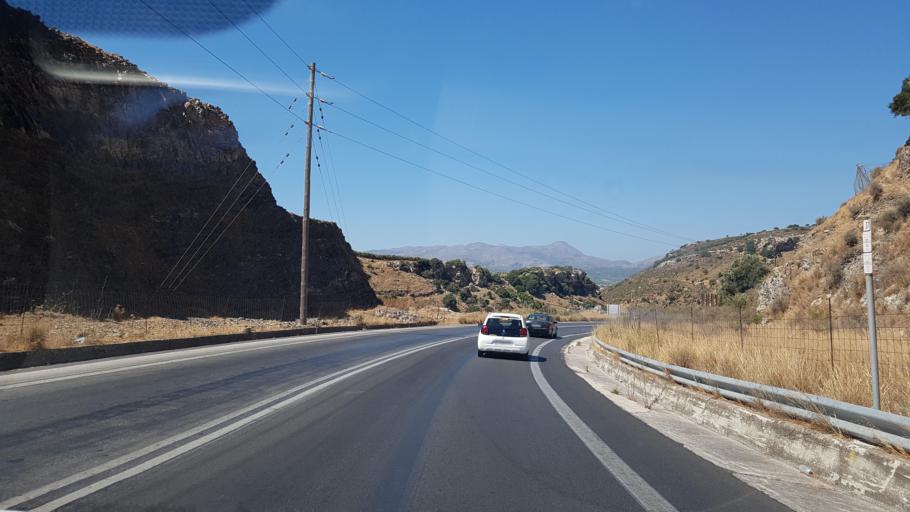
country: GR
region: Crete
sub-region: Nomos Chanias
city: Kolympari
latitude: 35.5149
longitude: 23.7407
